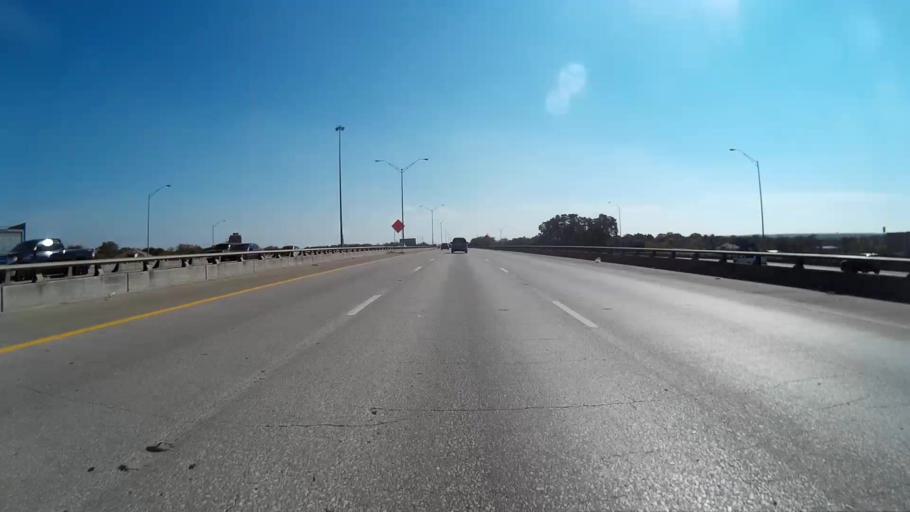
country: US
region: Texas
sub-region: Dallas County
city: Dallas
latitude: 32.7681
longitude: -96.7772
